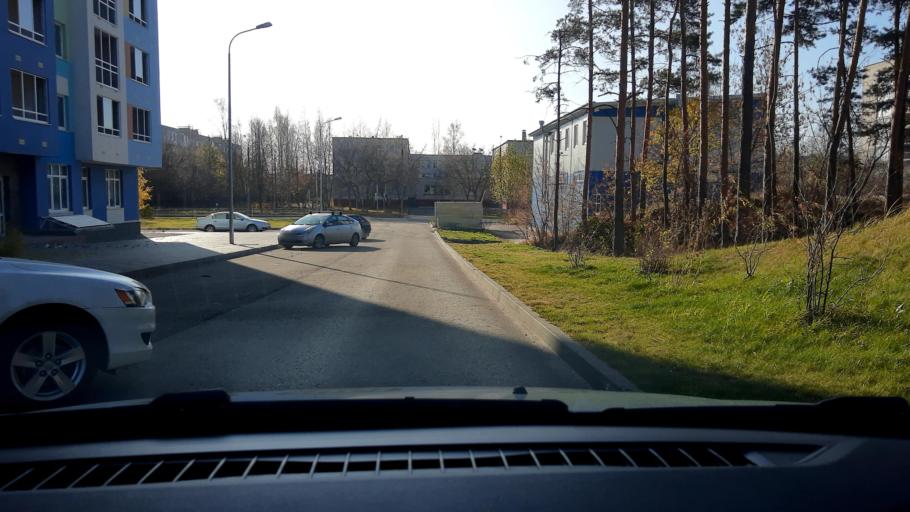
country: RU
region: Nizjnij Novgorod
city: Dzerzhinsk
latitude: 56.2571
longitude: 43.4585
